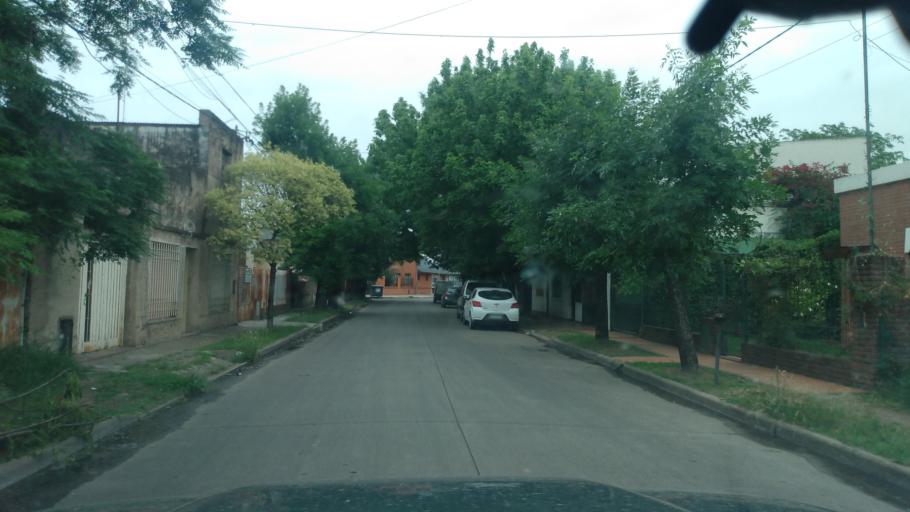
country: AR
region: Buenos Aires
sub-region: Partido de Lujan
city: Lujan
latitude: -34.5741
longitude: -59.1176
